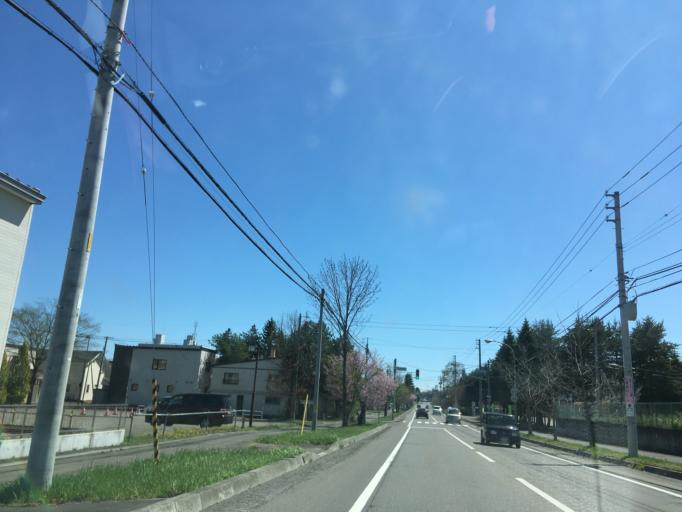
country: JP
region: Hokkaido
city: Obihiro
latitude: 42.9236
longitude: 143.1711
